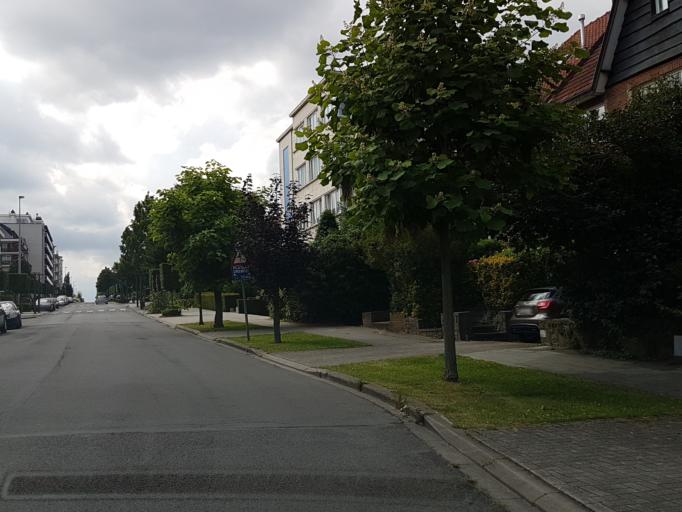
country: BE
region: Flanders
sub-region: Provincie Vlaams-Brabant
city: Kraainem
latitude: 50.8305
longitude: 4.4123
